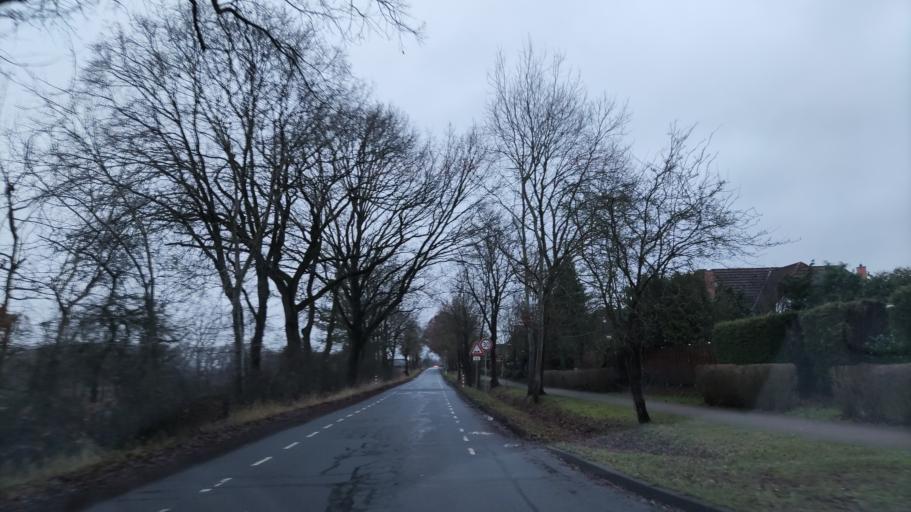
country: DE
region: Lower Saxony
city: Reppenstedt
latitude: 53.2544
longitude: 10.3533
